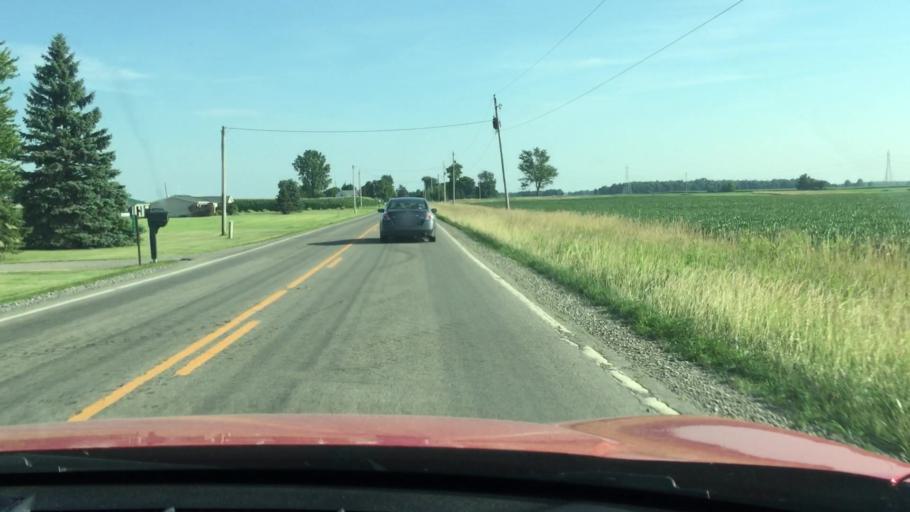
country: US
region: Ohio
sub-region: Hardin County
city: Ada
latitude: 40.6924
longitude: -83.8566
